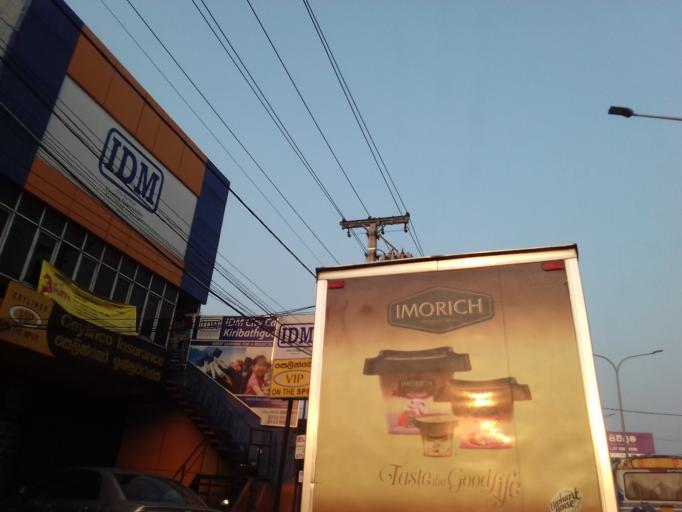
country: LK
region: Western
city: Kelaniya
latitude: 6.9745
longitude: 79.9227
